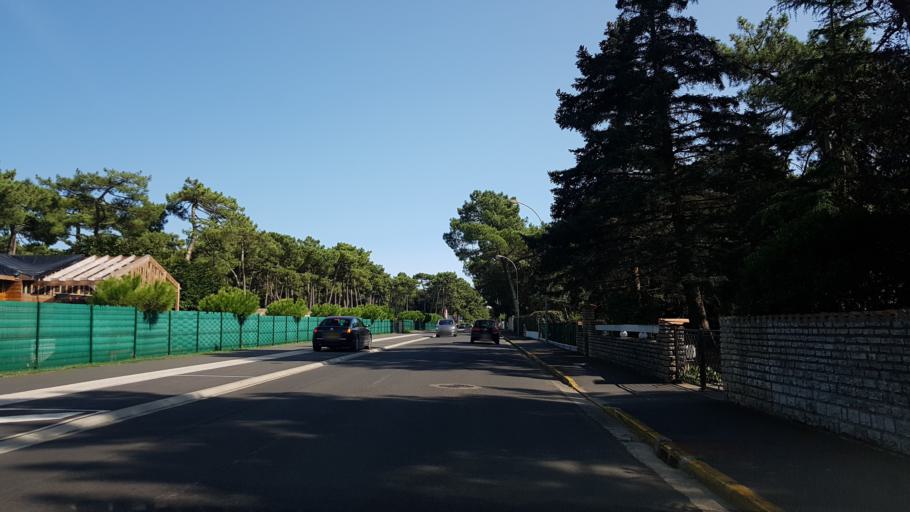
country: FR
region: Poitou-Charentes
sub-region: Departement de la Charente-Maritime
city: Les Mathes
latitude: 45.6932
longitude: -1.1868
